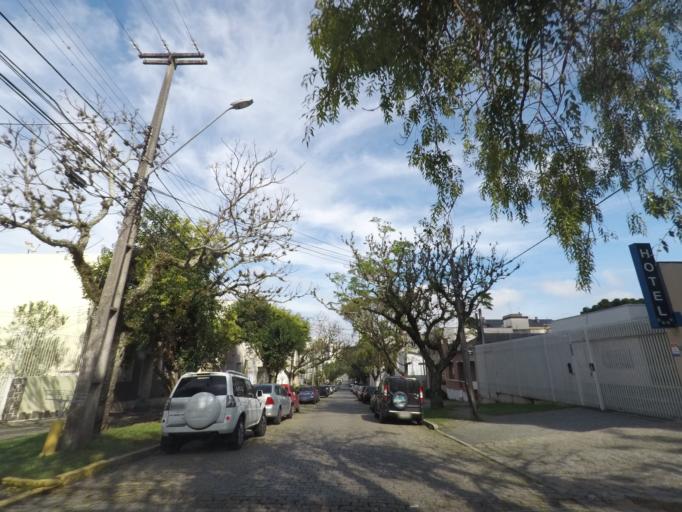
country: BR
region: Parana
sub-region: Curitiba
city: Curitiba
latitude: -25.4282
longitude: -49.2808
